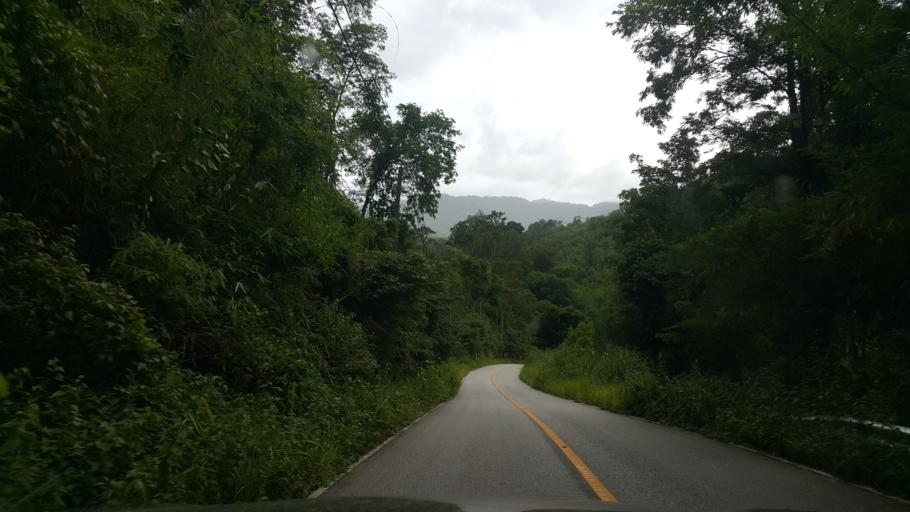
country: TH
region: Loei
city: Na Haeo
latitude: 17.5028
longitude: 100.8174
